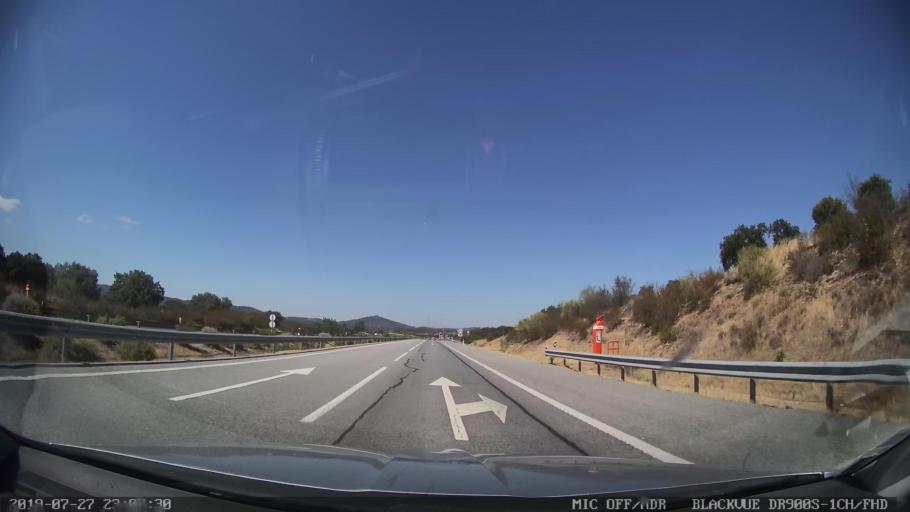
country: PT
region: Evora
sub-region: Estremoz
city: Estremoz
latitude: 38.8015
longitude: -7.6539
